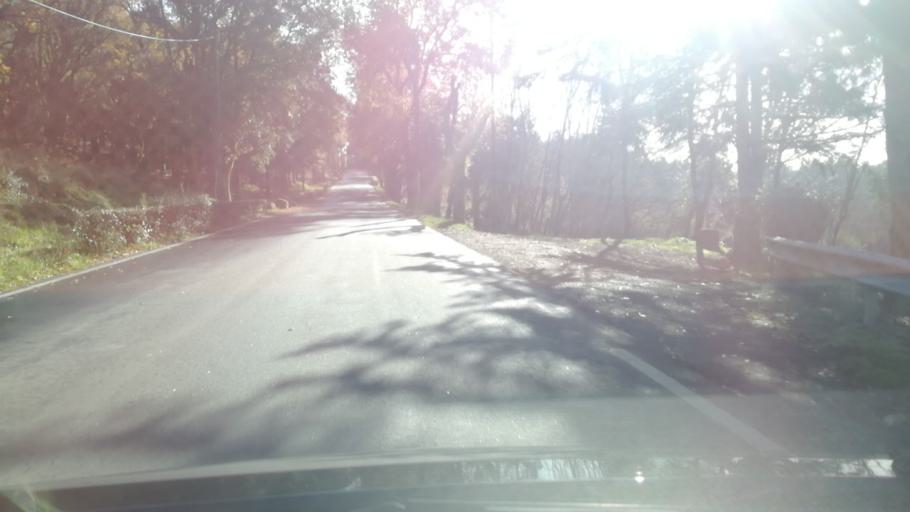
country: PT
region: Braga
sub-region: Braga
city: Braga
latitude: 41.5399
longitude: -8.3718
